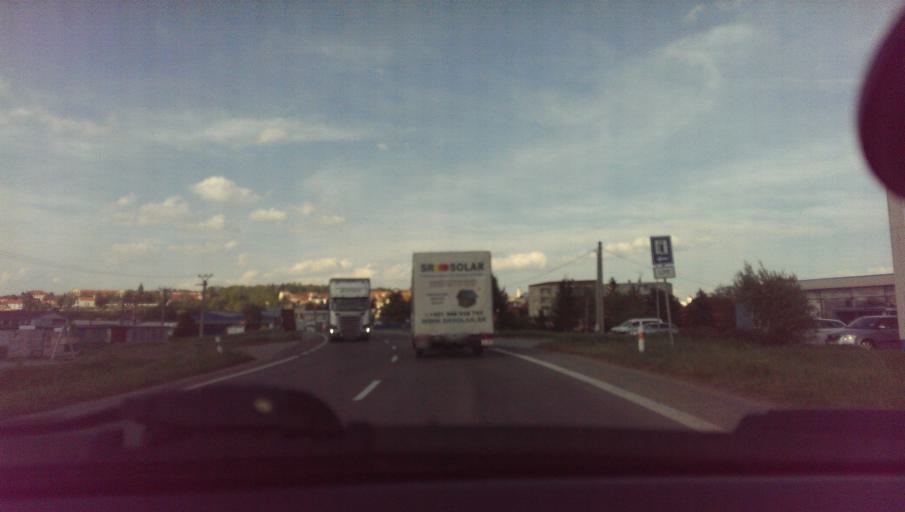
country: CZ
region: Zlin
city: Uhersky Brod
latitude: 49.0183
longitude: 17.6368
